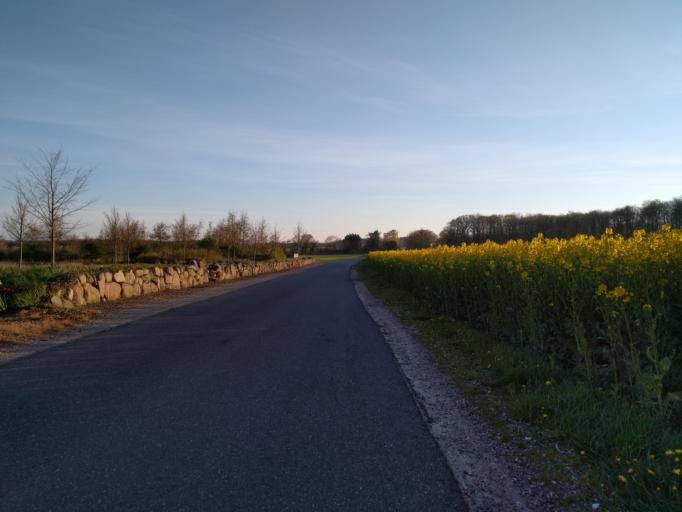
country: DK
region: South Denmark
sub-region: Kerteminde Kommune
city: Munkebo
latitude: 55.4157
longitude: 10.5588
